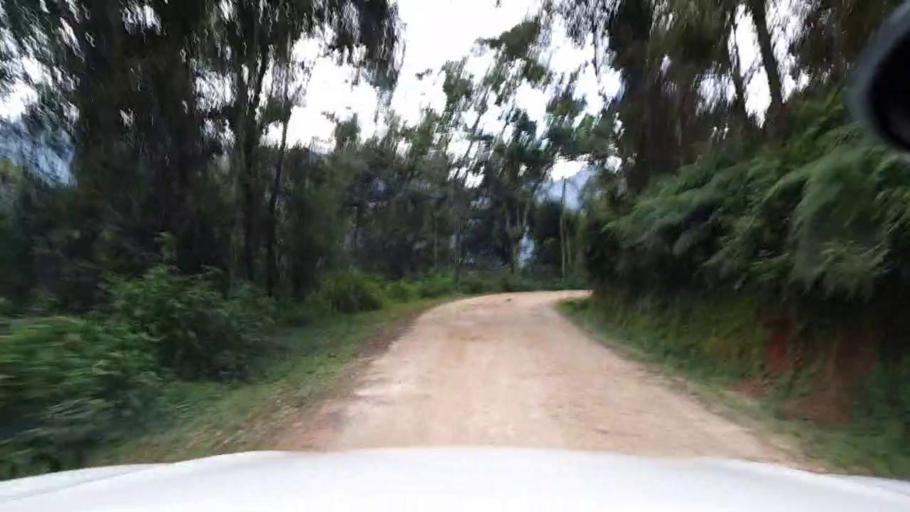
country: RW
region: Western Province
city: Cyangugu
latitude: -2.5642
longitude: 29.2279
